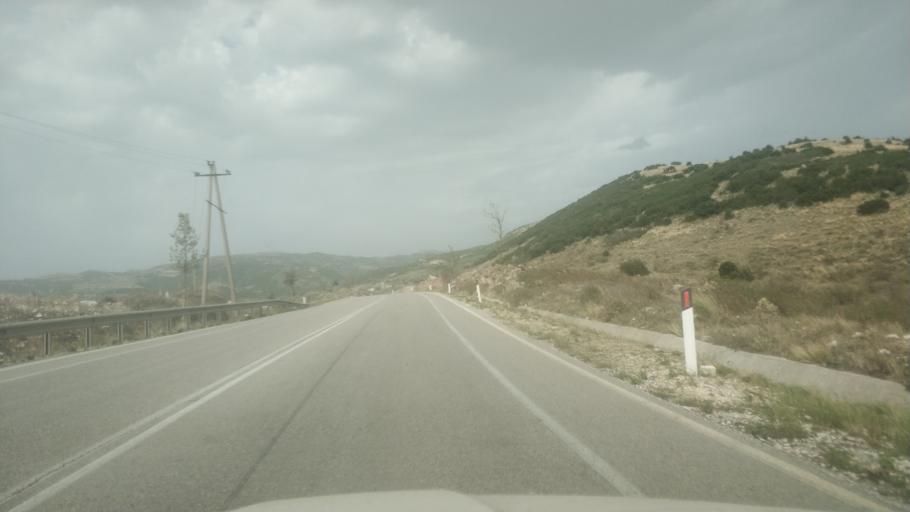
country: AL
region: Gjirokaster
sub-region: Rrethi i Tepelenes
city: Memaliaj
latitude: 40.3661
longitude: 19.9085
